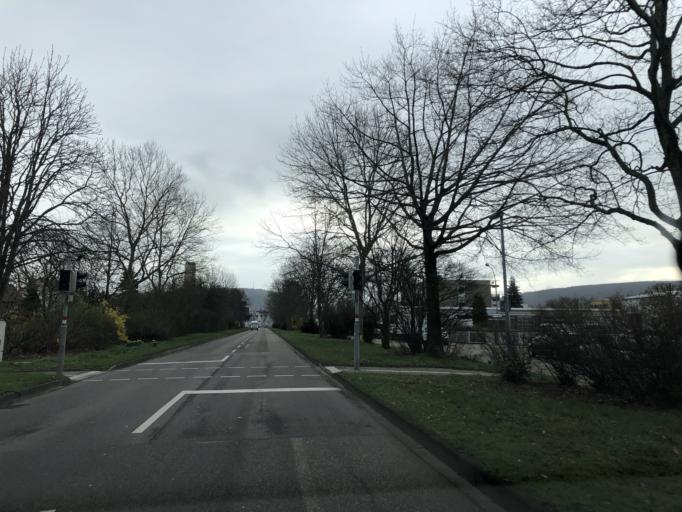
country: DE
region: Baden-Wuerttemberg
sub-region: Karlsruhe Region
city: Ettlingen
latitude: 48.9483
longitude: 8.3790
